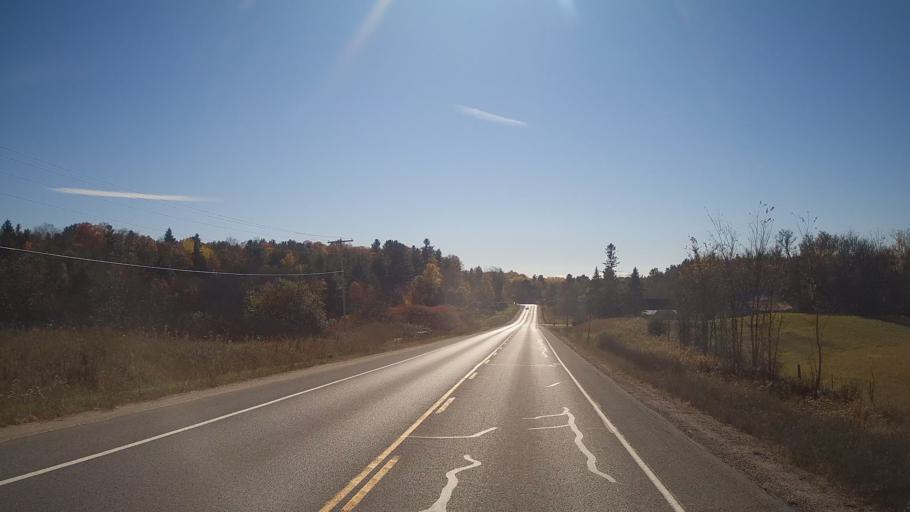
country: CA
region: Ontario
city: Kingston
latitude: 44.5538
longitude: -76.6747
